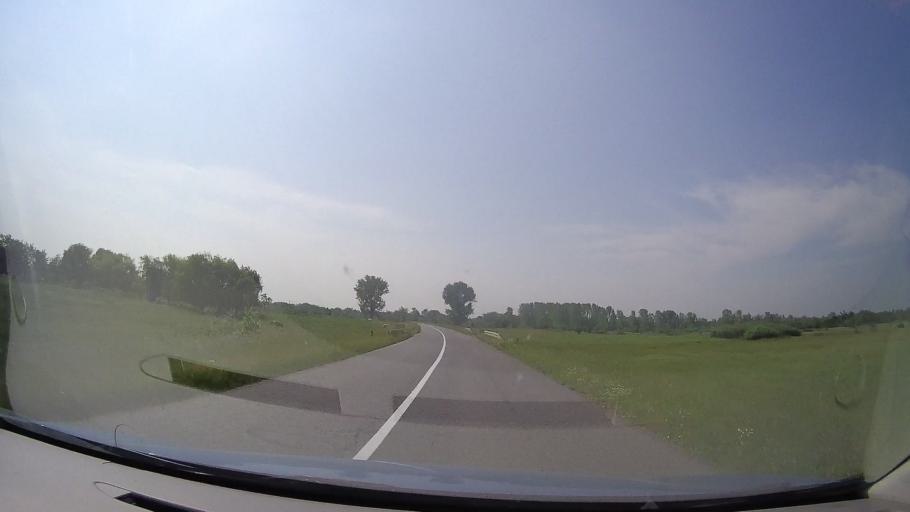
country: RS
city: Jarkovac
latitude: 45.2782
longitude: 20.7628
